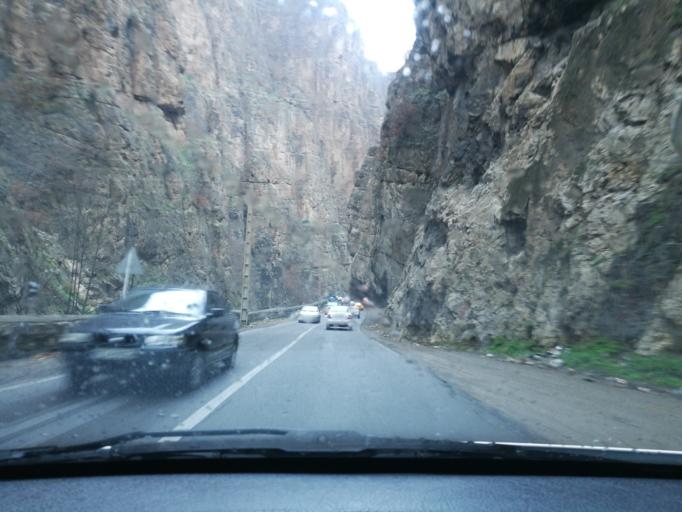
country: IR
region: Mazandaran
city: Chalus
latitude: 36.2715
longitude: 51.2450
